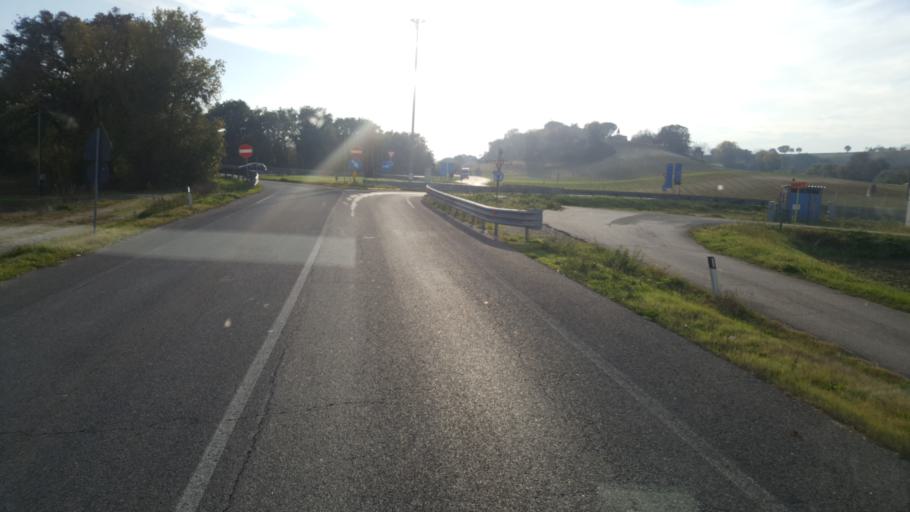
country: IT
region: The Marches
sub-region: Provincia di Ancona
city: Casine
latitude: 43.6424
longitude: 13.1403
